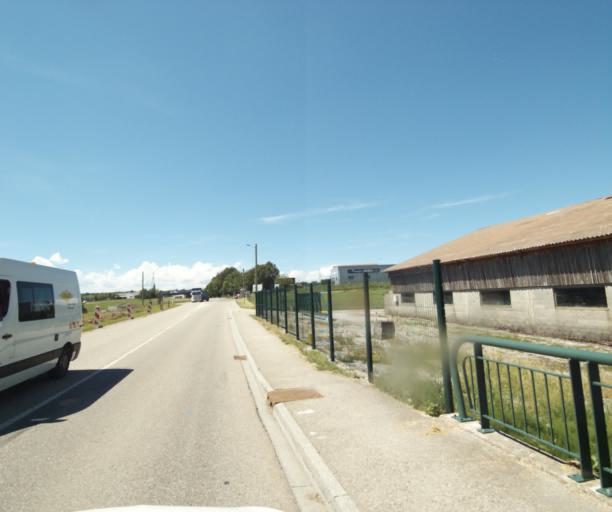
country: FR
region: Rhone-Alpes
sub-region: Departement de la Haute-Savoie
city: Bons-en-Chablais
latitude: 46.2716
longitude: 6.3529
